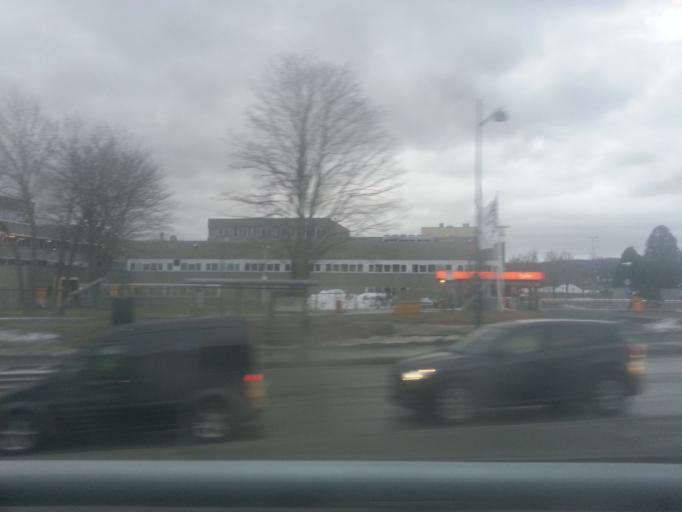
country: NO
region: Sor-Trondelag
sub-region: Trondheim
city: Trondheim
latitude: 63.4336
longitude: 10.4562
